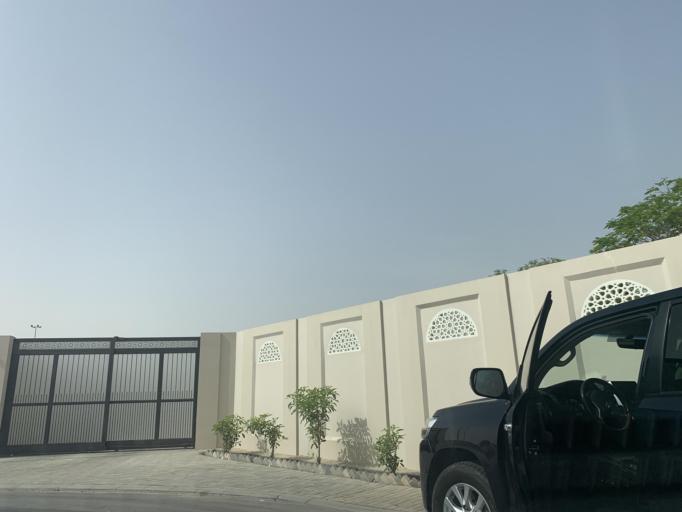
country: BH
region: Central Governorate
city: Madinat Hamad
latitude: 26.1399
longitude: 50.5155
